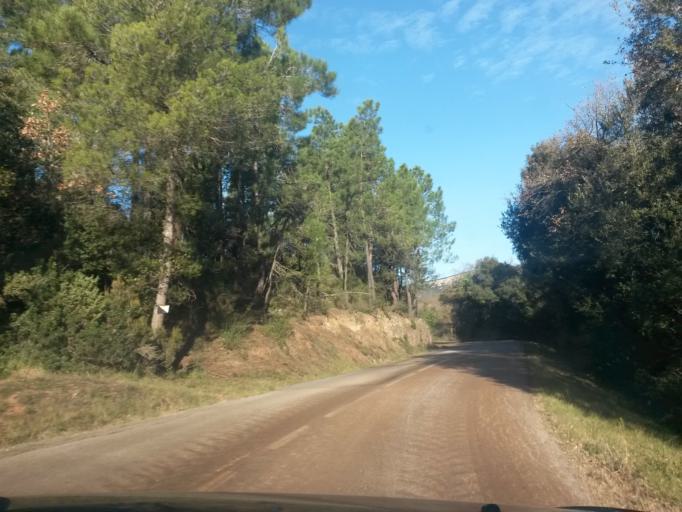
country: ES
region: Catalonia
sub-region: Provincia de Girona
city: la Cellera de Ter
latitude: 42.0121
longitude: 2.6739
